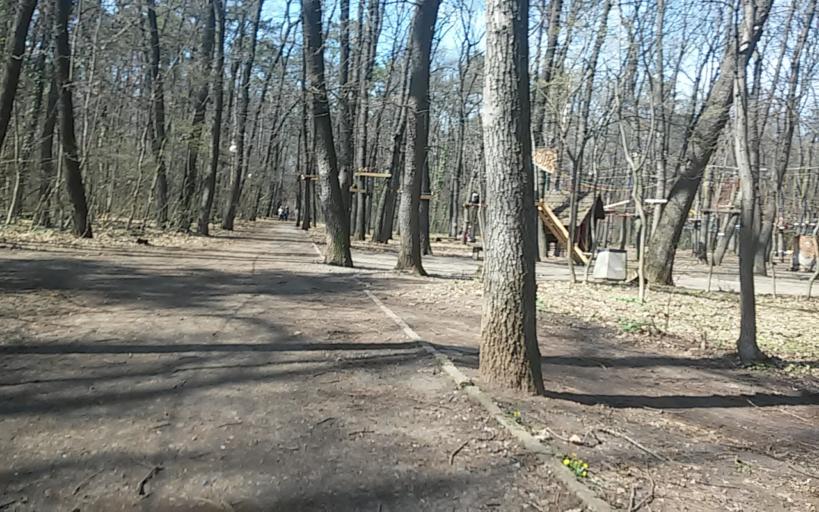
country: BG
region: Sofia-Capital
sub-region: Stolichna Obshtina
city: Sofia
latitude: 42.6775
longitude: 23.3524
